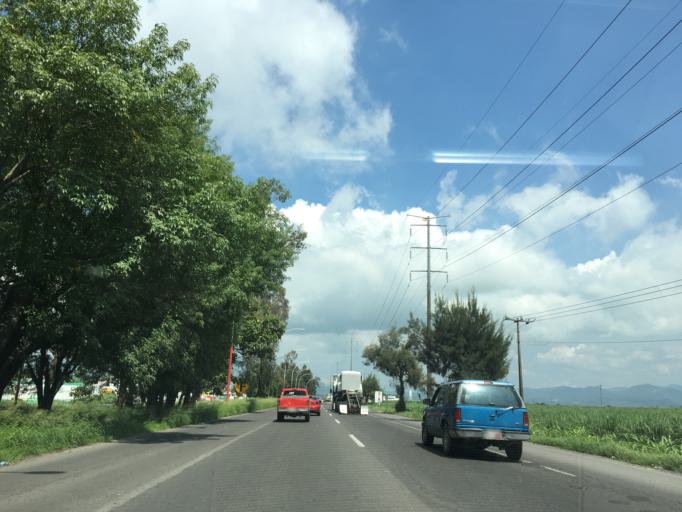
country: MX
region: Nayarit
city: Xalisco
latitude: 21.4665
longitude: -104.8813
